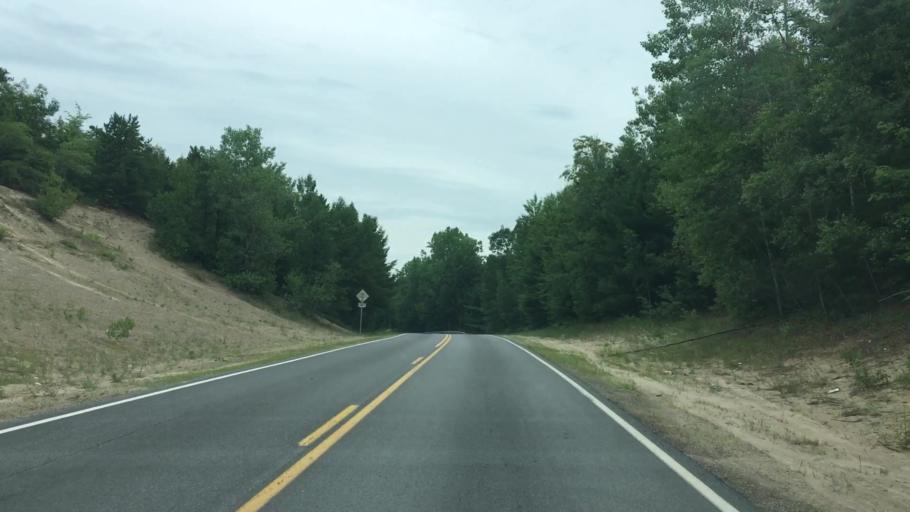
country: US
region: New York
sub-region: Essex County
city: Keeseville
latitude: 44.4753
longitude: -73.5951
